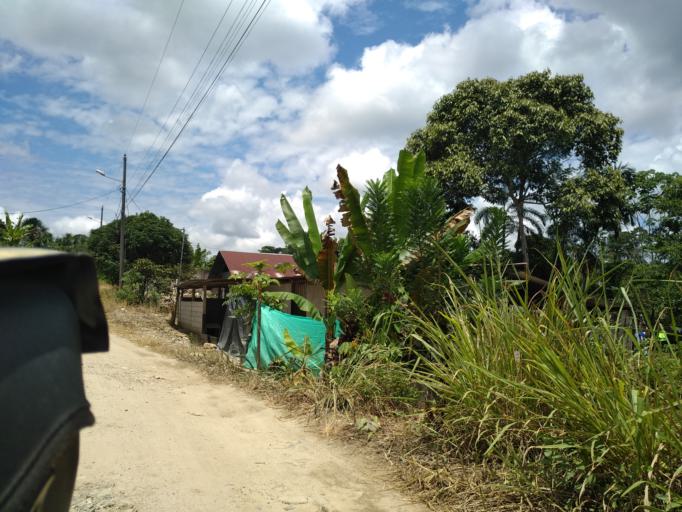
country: EC
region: Napo
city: Tena
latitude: -0.9929
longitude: -77.8237
